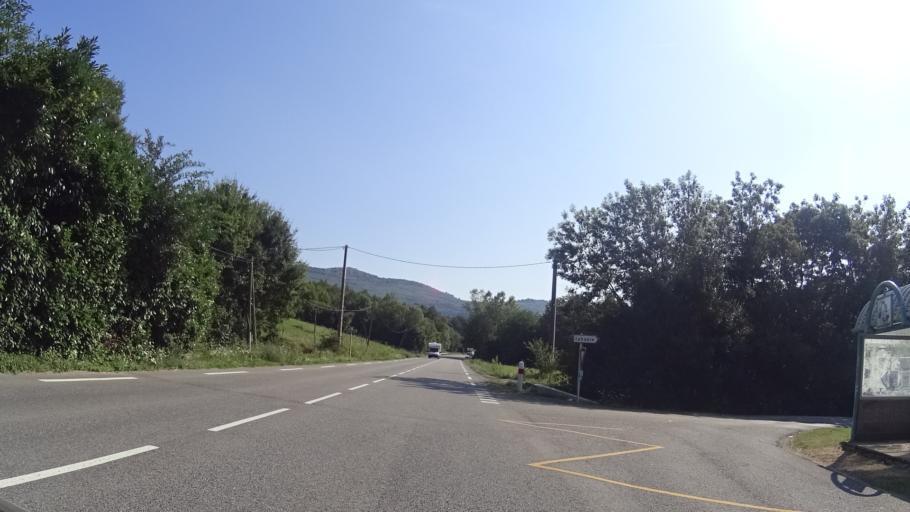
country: FR
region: Midi-Pyrenees
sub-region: Departement de l'Ariege
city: Saint-Paul-de-Jarrat
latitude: 42.9319
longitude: 1.7081
